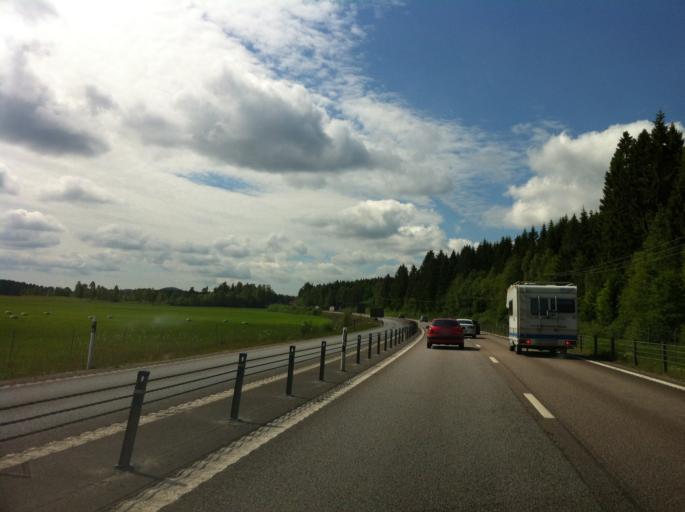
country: SE
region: Vaermland
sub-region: Grums Kommun
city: Grums
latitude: 59.3627
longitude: 13.1349
